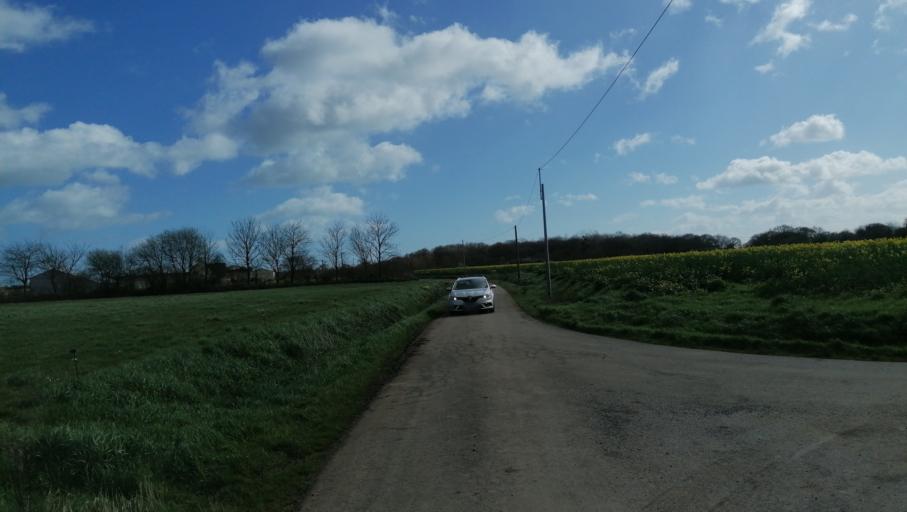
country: FR
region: Brittany
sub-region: Departement des Cotes-d'Armor
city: Pleguien
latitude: 48.6394
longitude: -2.9289
